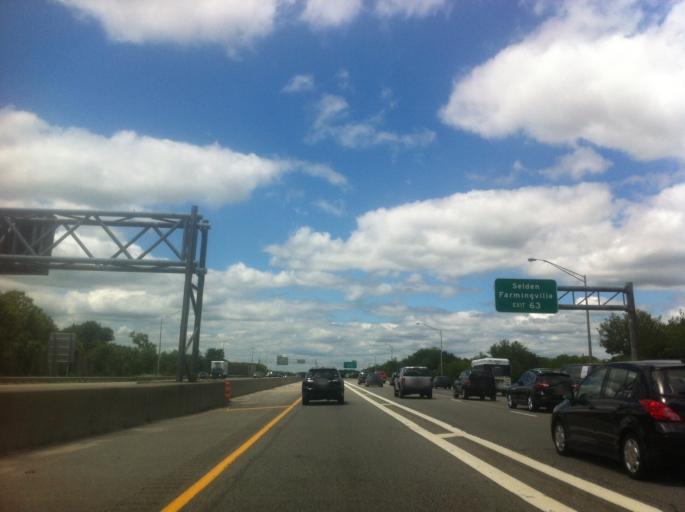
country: US
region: New York
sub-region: Suffolk County
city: Medford
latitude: 40.8237
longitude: -73.0100
